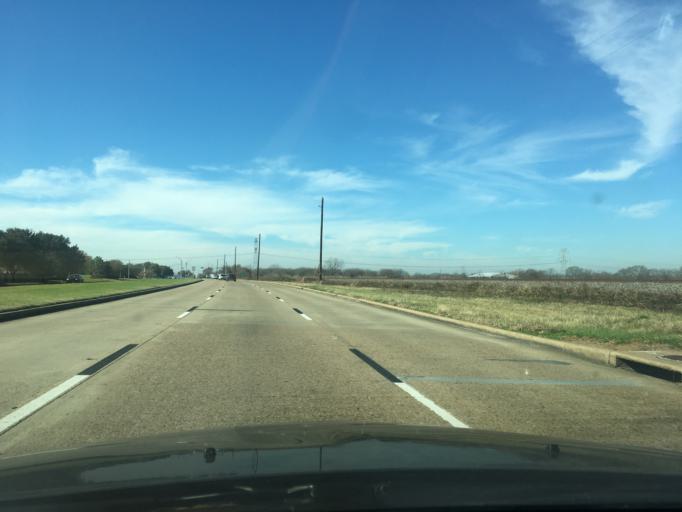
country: US
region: Texas
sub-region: Fort Bend County
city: New Territory
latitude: 29.6014
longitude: -95.6881
